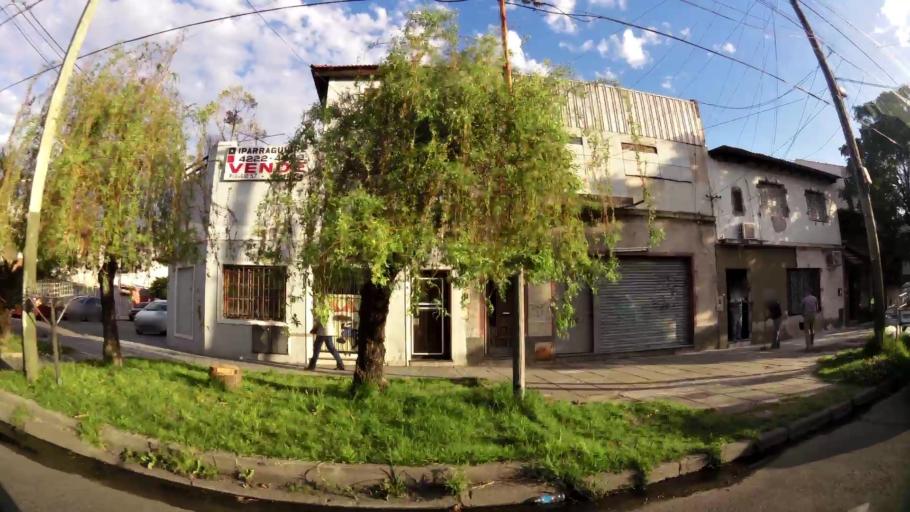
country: AR
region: Buenos Aires
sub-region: Partido de Avellaneda
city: Avellaneda
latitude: -34.6805
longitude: -58.3477
